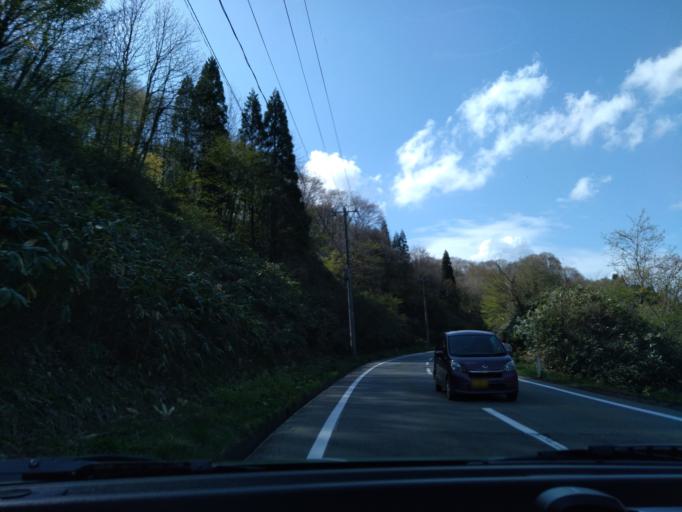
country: JP
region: Akita
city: Akita
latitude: 39.6924
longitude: 140.2234
